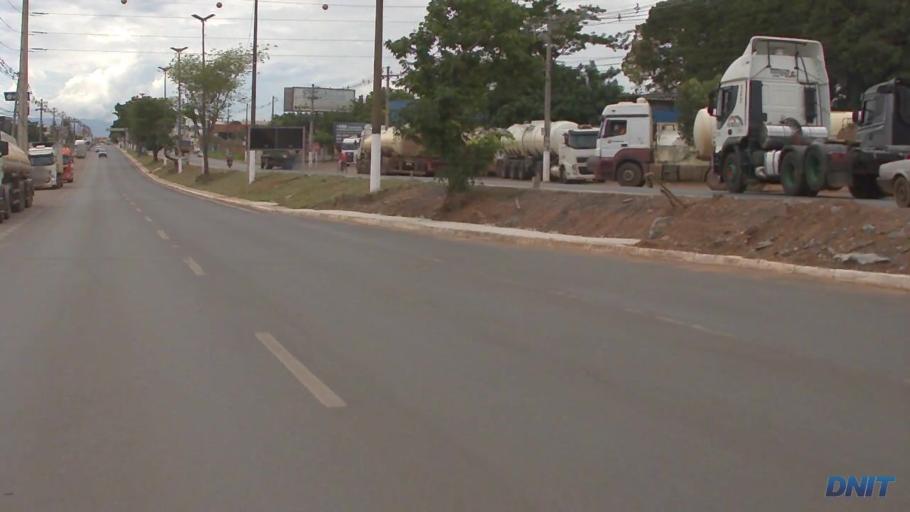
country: BR
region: Mato Grosso
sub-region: Varzea Grande
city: Varzea Grande
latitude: -15.6478
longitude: -56.1914
